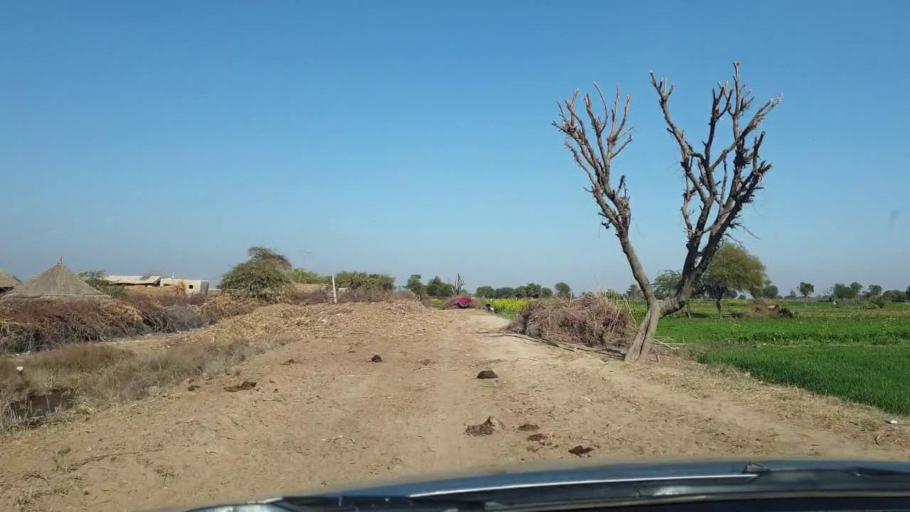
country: PK
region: Sindh
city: Jhol
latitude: 25.9361
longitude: 68.9499
